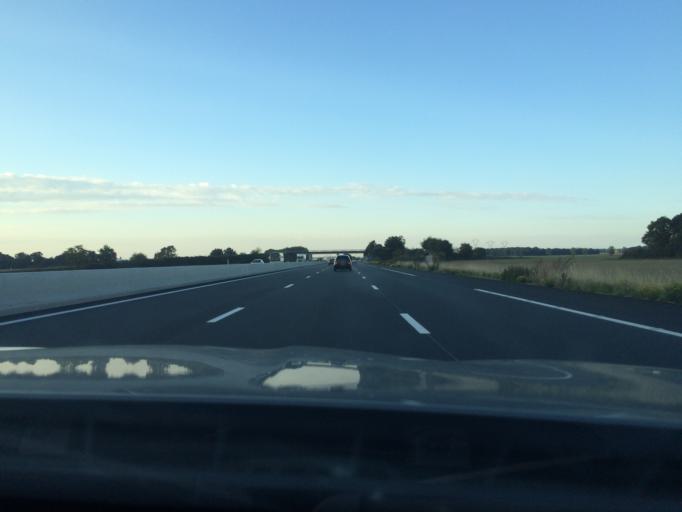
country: FR
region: Ile-de-France
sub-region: Departement de l'Essonne
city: Soisy-sur-Ecole
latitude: 48.5149
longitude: 2.5069
